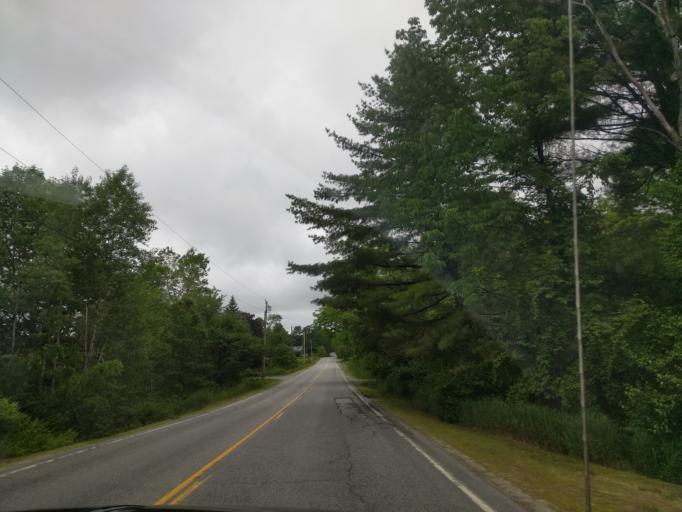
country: US
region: Maine
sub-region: Cumberland County
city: North Windham
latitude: 43.8291
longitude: -70.3966
